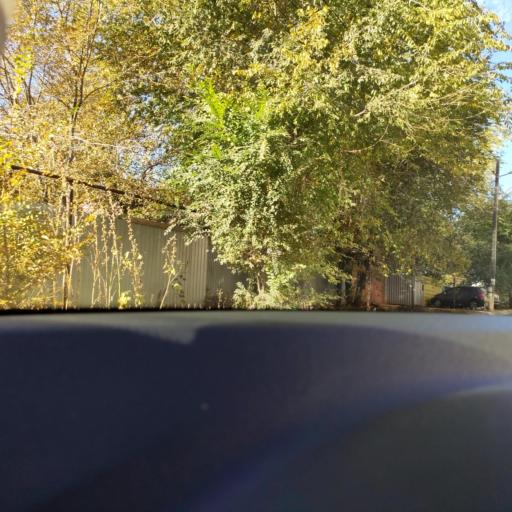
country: RU
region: Samara
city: Samara
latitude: 53.2298
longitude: 50.2459
